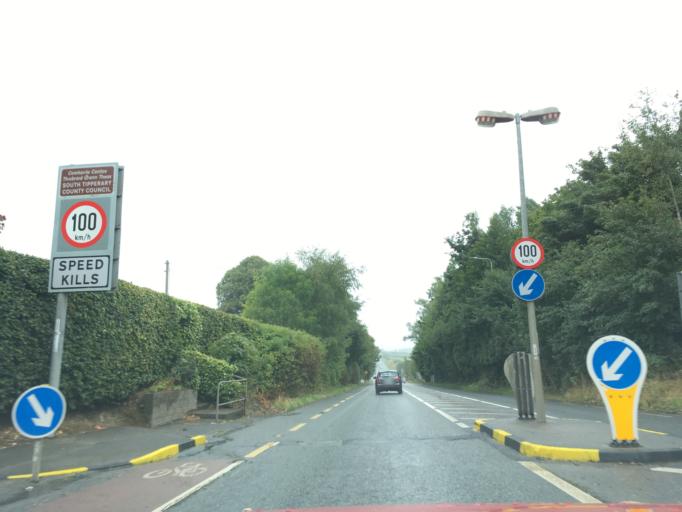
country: IE
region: Munster
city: Carrick-on-Suir
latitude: 52.3522
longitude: -7.3847
